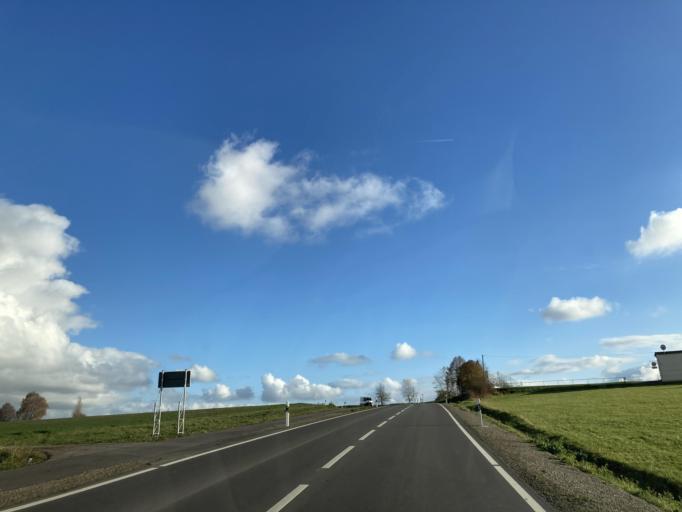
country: DE
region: Baden-Wuerttemberg
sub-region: Freiburg Region
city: Muhlheim am Bach
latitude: 48.4060
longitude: 8.6690
